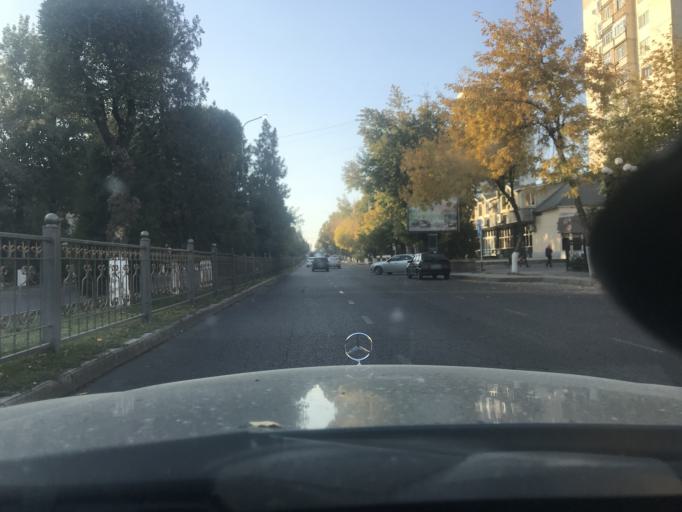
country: KZ
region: Ongtustik Qazaqstan
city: Shymkent
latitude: 42.3000
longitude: 69.6085
